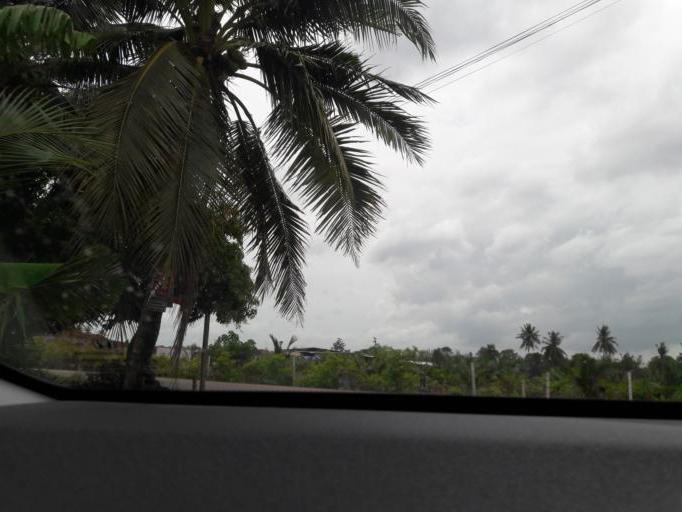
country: TH
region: Ratchaburi
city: Damnoen Saduak
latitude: 13.5684
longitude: 99.9833
